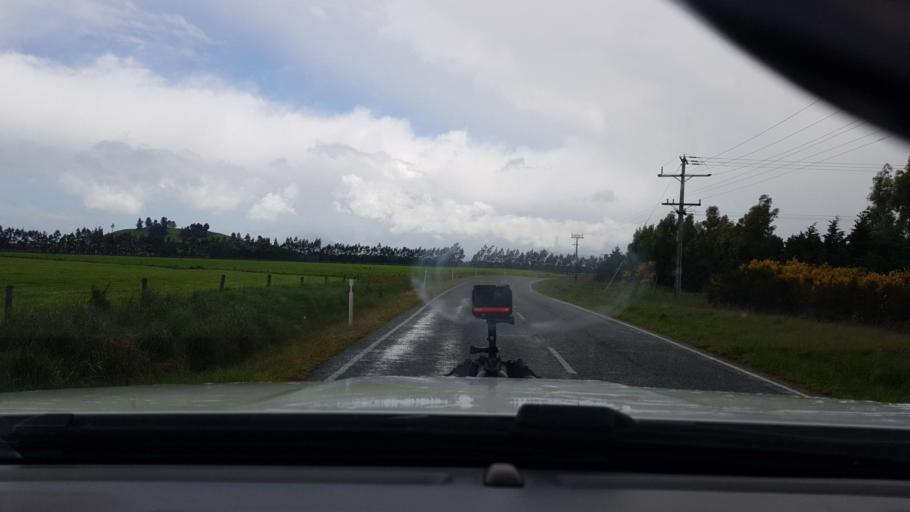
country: NZ
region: Southland
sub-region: Southland District
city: Winton
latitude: -45.7421
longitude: 168.3970
